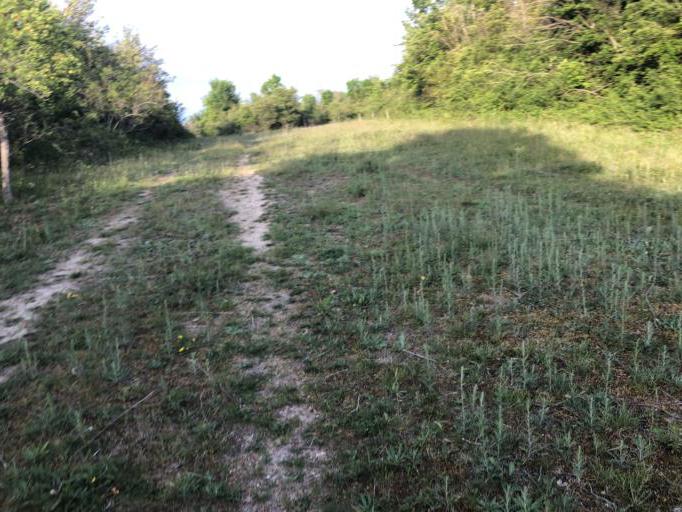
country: DE
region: Saxony-Anhalt
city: Balgstadt
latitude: 51.1963
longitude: 11.7439
